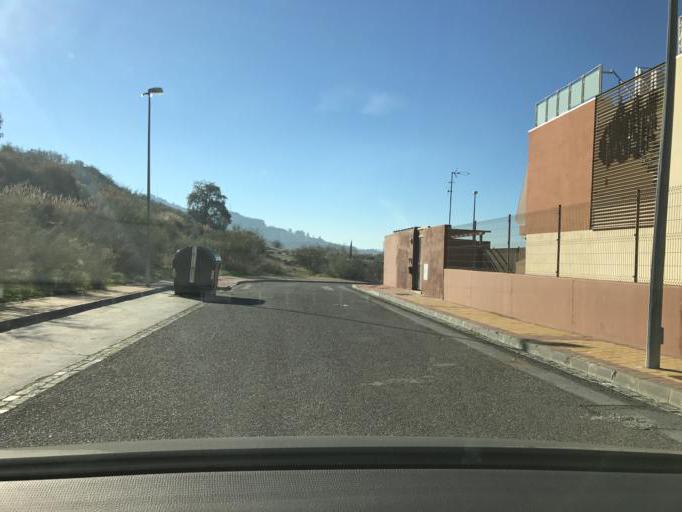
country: ES
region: Andalusia
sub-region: Provincia de Granada
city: Jun
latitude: 37.2106
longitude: -3.5915
